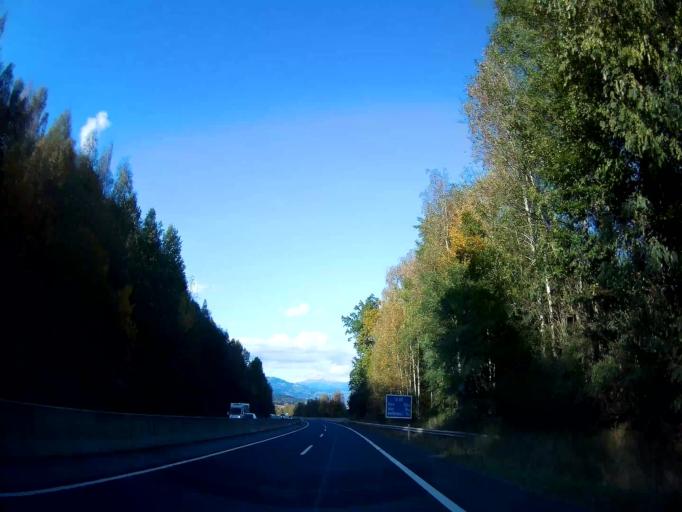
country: AT
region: Carinthia
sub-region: Politischer Bezirk Wolfsberg
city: Sankt Andrae
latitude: 46.7539
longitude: 14.8163
